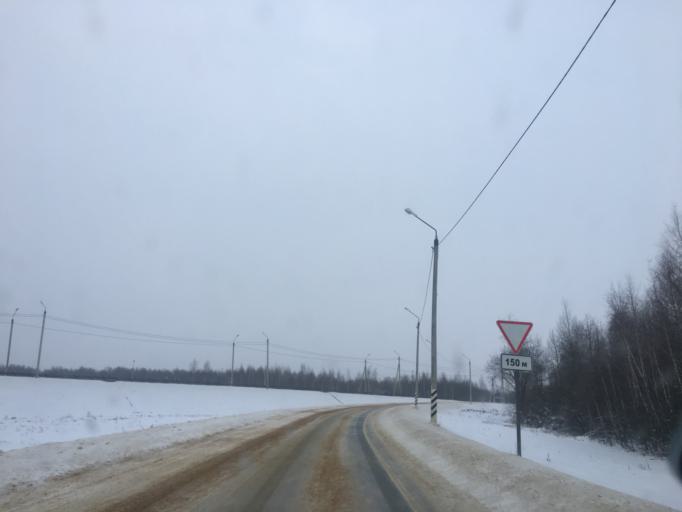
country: RU
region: Tula
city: Kosaya Gora
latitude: 54.1576
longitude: 37.4941
